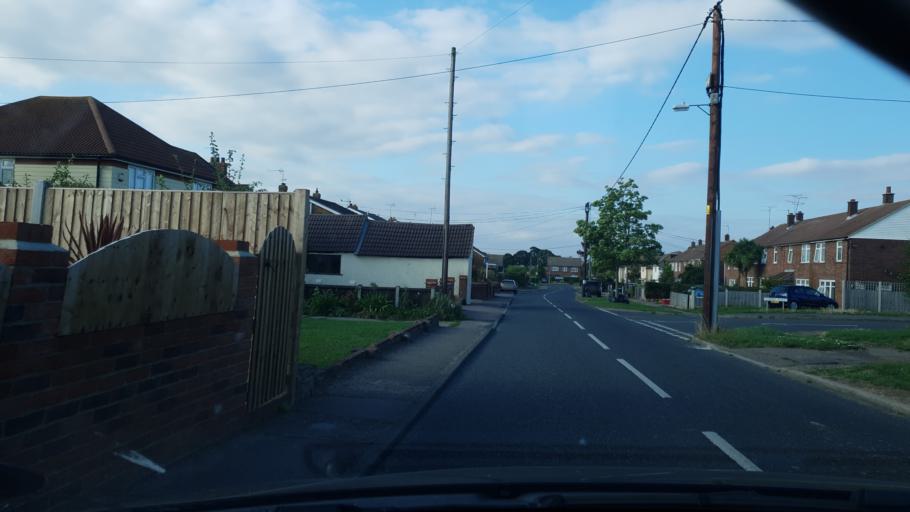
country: GB
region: England
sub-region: Essex
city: Frinton-on-Sea
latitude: 51.8505
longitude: 1.2247
